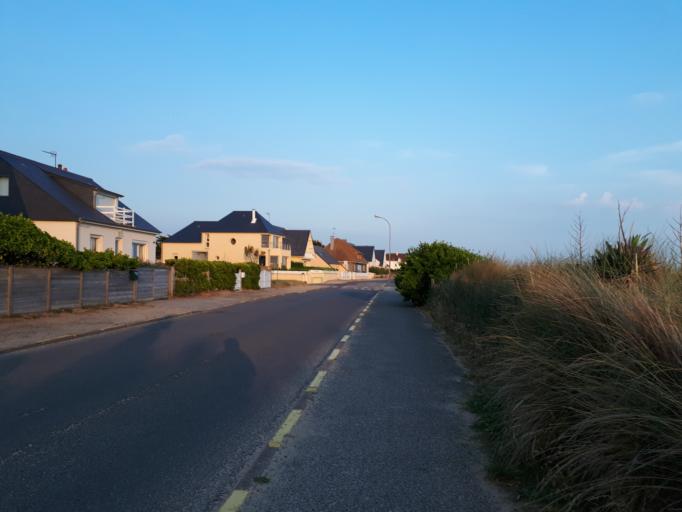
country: FR
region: Lower Normandy
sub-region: Departement de la Manche
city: Barneville-Plage
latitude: 49.3638
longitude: -1.7651
